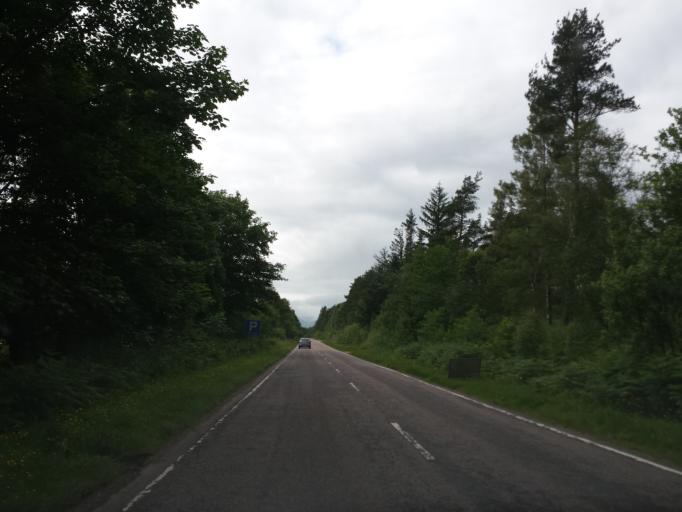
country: GB
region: Scotland
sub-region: Highland
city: Fort William
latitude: 56.8558
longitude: -5.1987
